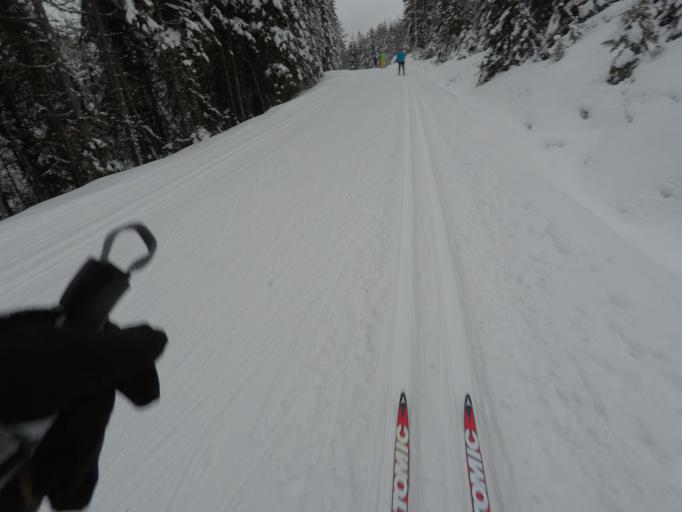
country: SE
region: Dalarna
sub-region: Ludvika Kommun
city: Abborrberget
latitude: 60.1359
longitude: 14.4833
